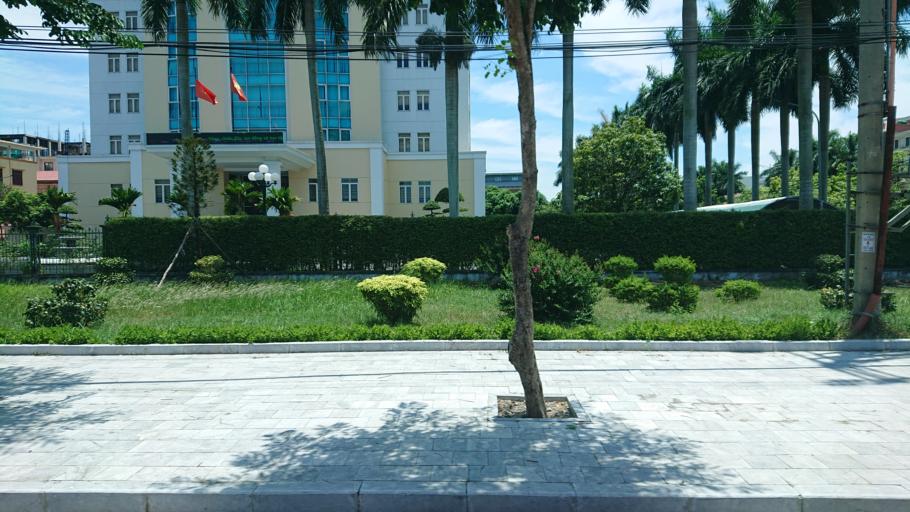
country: VN
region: Ninh Binh
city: Thanh Pho Ninh Binh
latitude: 20.2681
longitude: 105.9724
